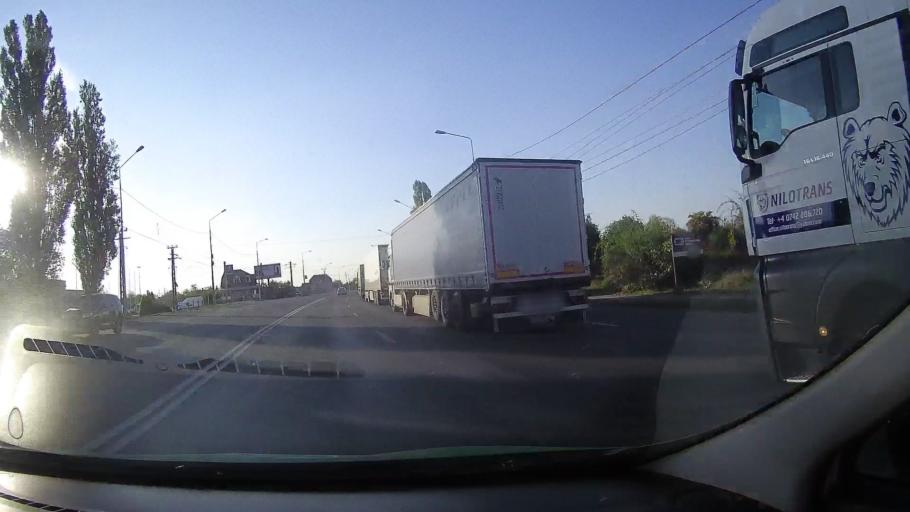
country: RO
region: Bihor
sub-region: Comuna Bors
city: Santion
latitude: 47.1009
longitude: 21.8442
